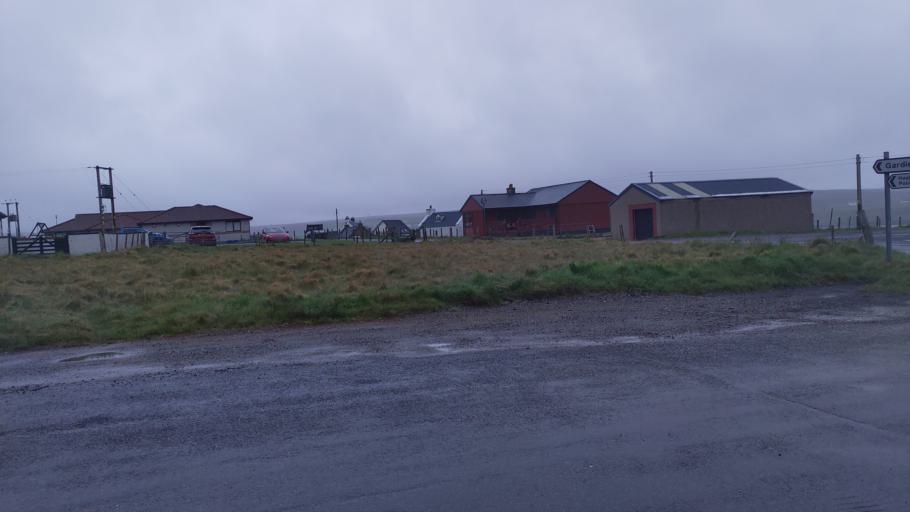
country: GB
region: Scotland
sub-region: Shetland Islands
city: Shetland
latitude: 60.5996
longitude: -1.0678
